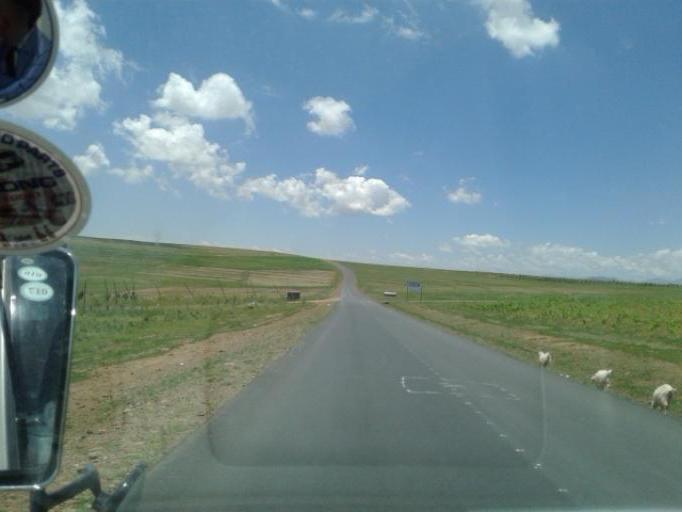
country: LS
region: Maseru
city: Maseru
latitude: -29.3078
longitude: 27.6035
